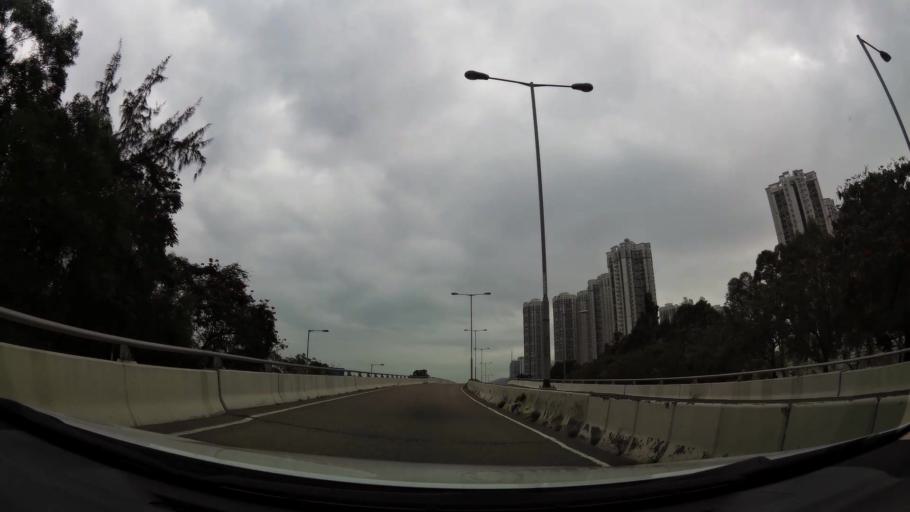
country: HK
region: Yuen Long
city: Yuen Long Kau Hui
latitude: 22.4631
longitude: 114.0085
